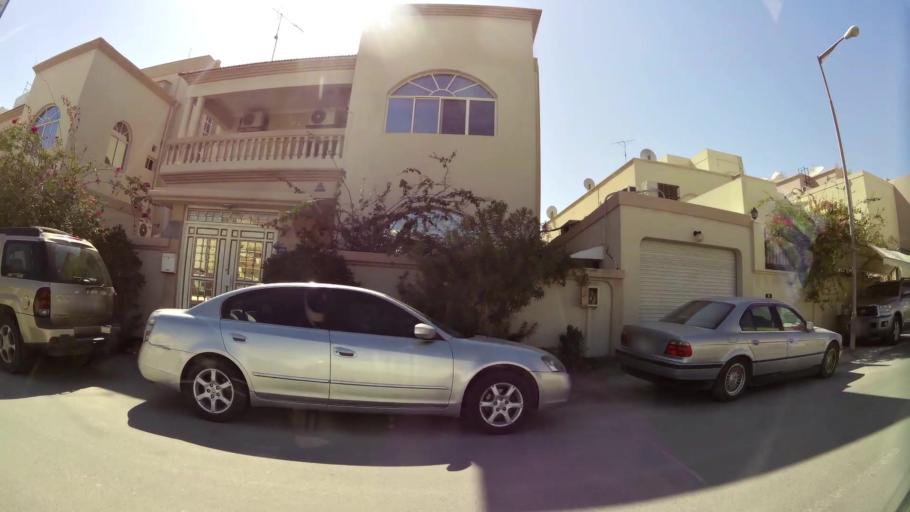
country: BH
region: Manama
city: Manama
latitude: 26.2059
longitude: 50.5793
